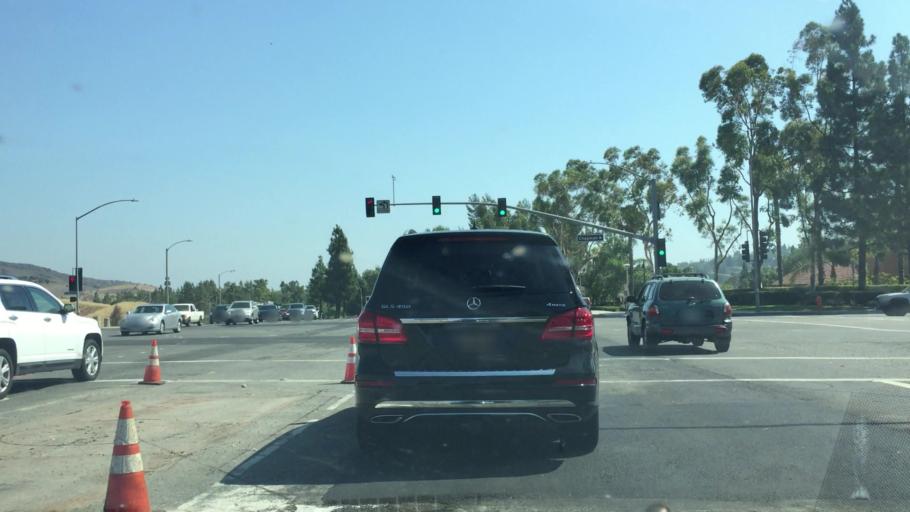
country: US
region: California
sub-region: Orange County
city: North Tustin
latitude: 33.7927
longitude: -117.7614
